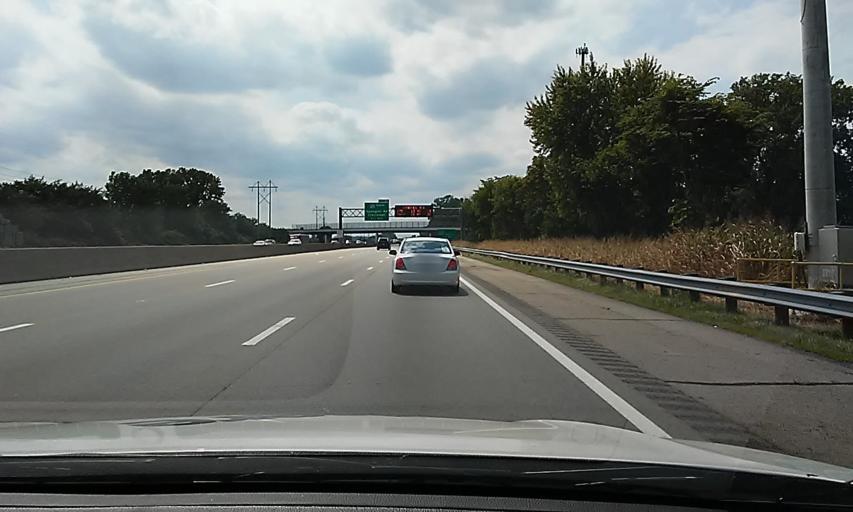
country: US
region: Ohio
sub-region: Clark County
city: Green Meadows
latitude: 39.8783
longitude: -83.9626
